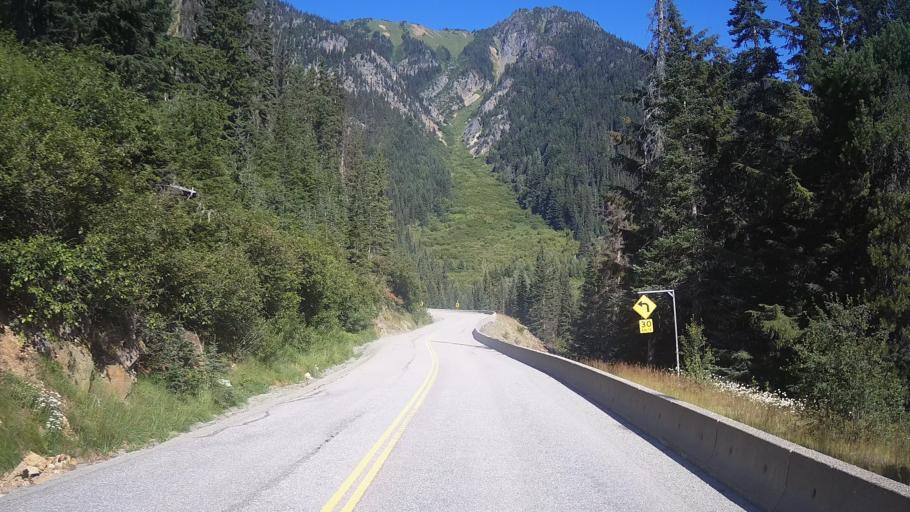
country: CA
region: British Columbia
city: Lillooet
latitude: 50.4313
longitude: -122.2574
